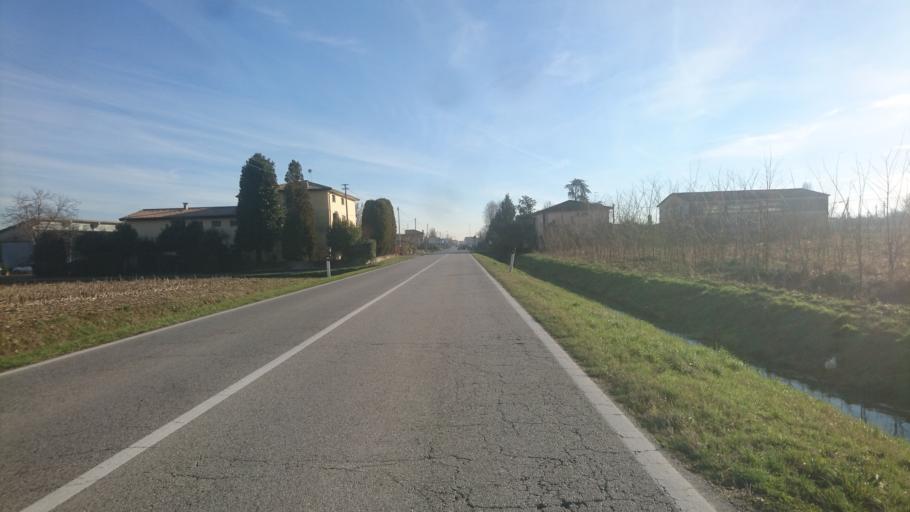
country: IT
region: Veneto
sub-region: Provincia di Padova
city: Villafranca Padovana
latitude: 45.5020
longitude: 11.7933
